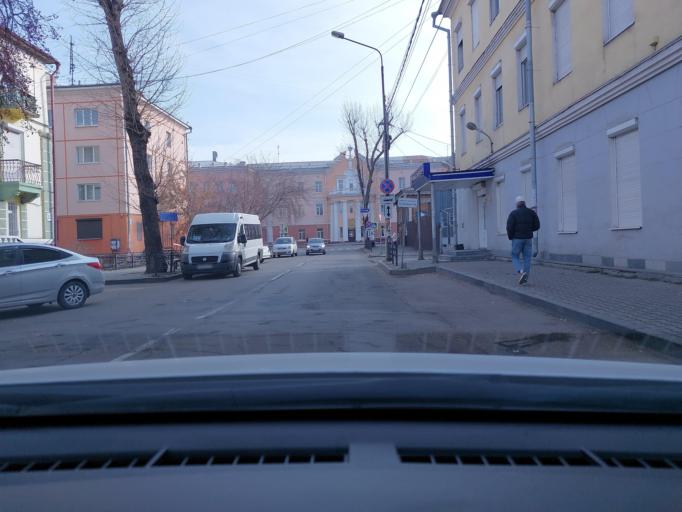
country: RU
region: Irkutsk
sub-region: Irkutskiy Rayon
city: Irkutsk
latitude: 52.2800
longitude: 104.2924
